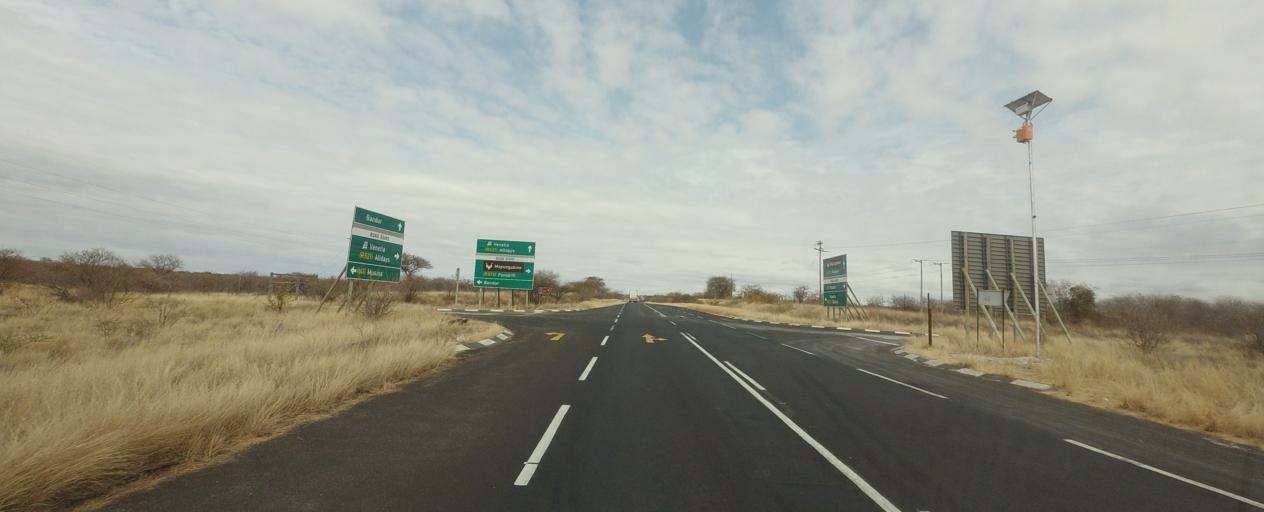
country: ZW
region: Matabeleland South
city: Beitbridge
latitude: -22.4295
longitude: 29.4202
